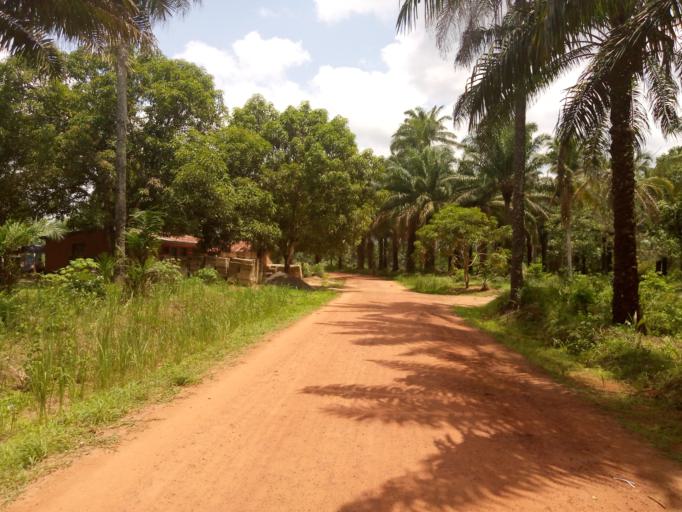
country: SL
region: Western Area
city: Waterloo
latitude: 8.3799
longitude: -12.9683
